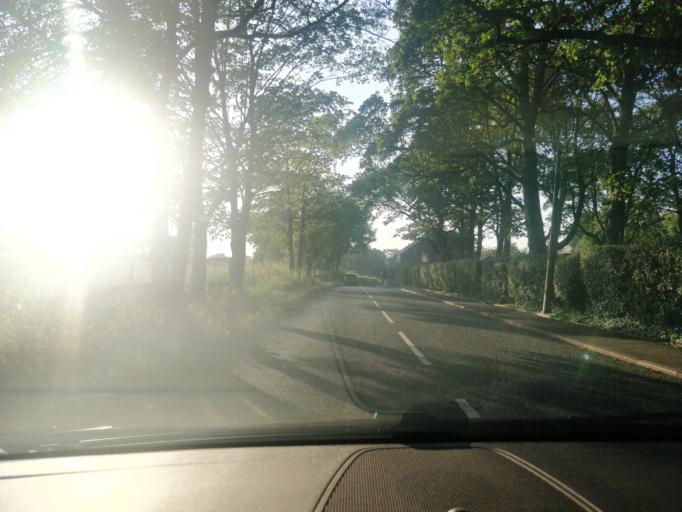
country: GB
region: England
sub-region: Lancashire
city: Parbold
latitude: 53.5815
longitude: -2.7709
